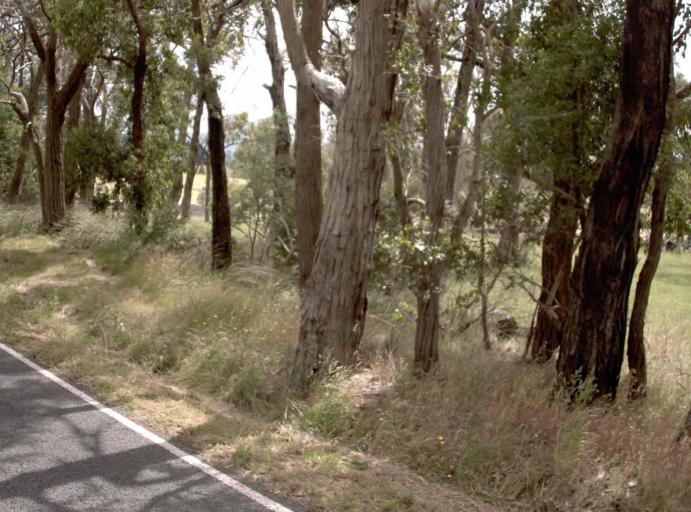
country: AU
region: Victoria
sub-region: Latrobe
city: Moe
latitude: -38.1253
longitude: 146.1484
